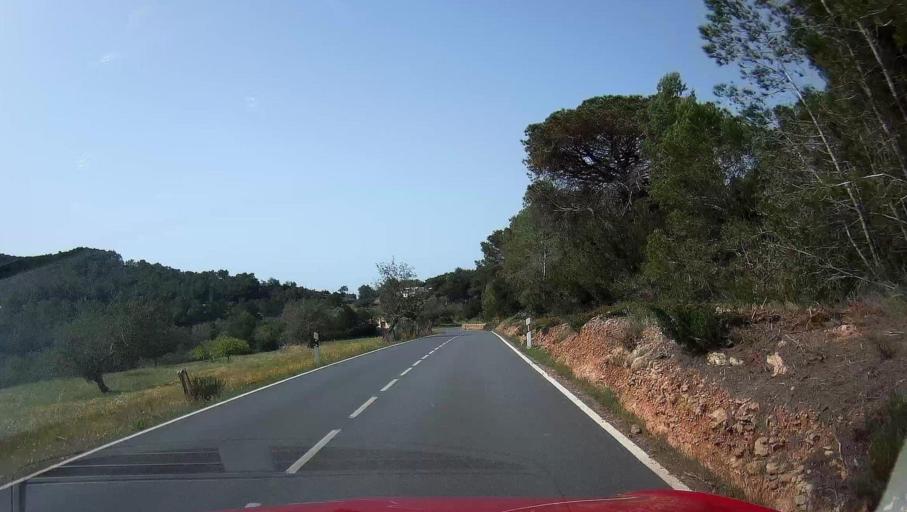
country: ES
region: Balearic Islands
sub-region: Illes Balears
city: Sant Joan de Labritja
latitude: 39.0436
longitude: 1.5674
